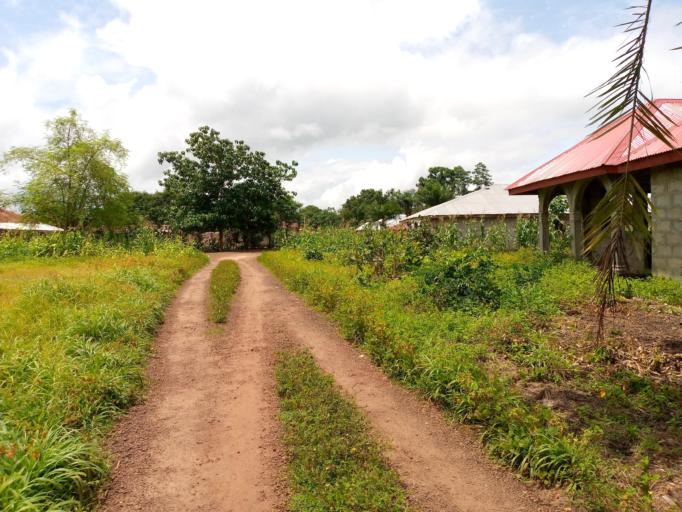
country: SL
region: Northern Province
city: Magburaka
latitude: 8.7279
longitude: -11.9282
